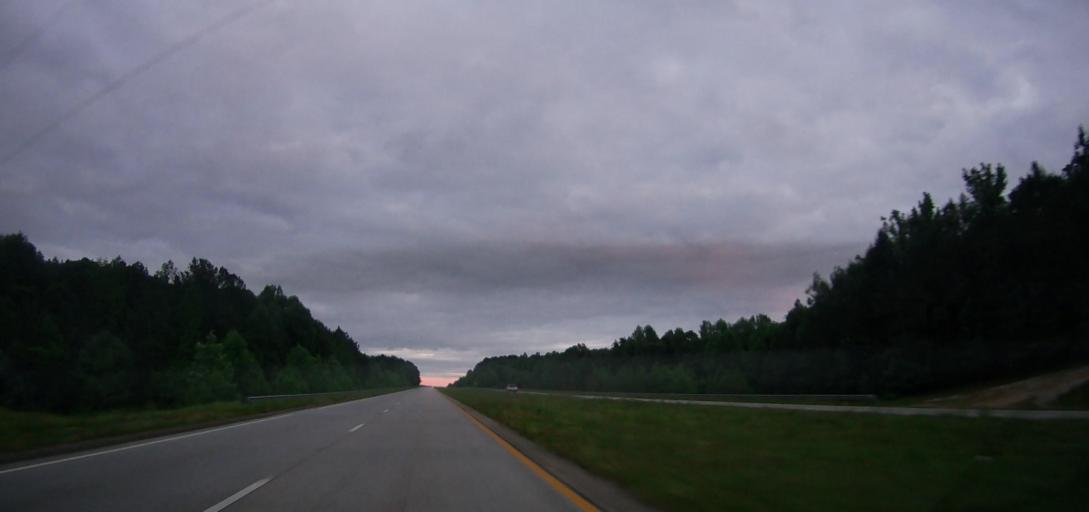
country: US
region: Georgia
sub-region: Jackson County
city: Jefferson
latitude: 34.0971
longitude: -83.5885
